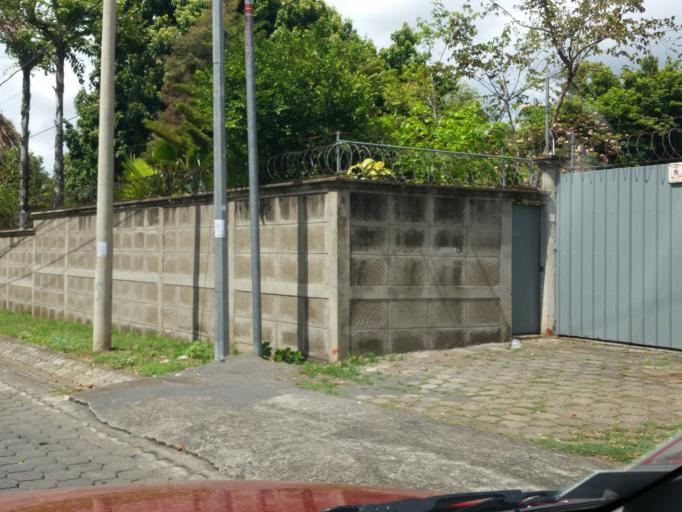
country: NI
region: Managua
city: Managua
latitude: 12.0839
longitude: -86.2322
